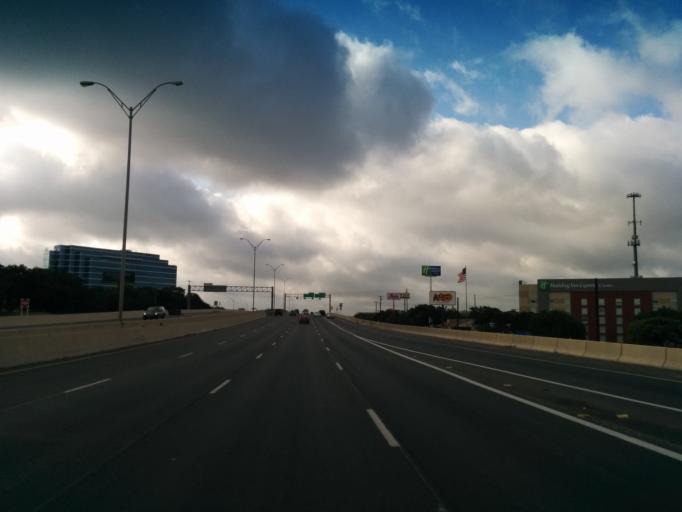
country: US
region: Texas
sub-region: Bexar County
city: Shavano Park
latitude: 29.5464
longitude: -98.5820
